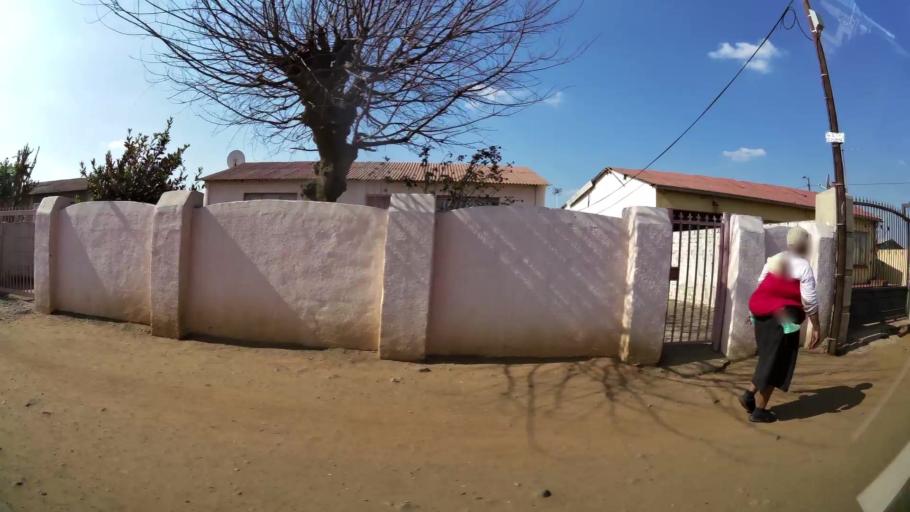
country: ZA
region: Gauteng
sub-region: Ekurhuleni Metropolitan Municipality
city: Benoni
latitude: -26.1486
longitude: 28.4050
